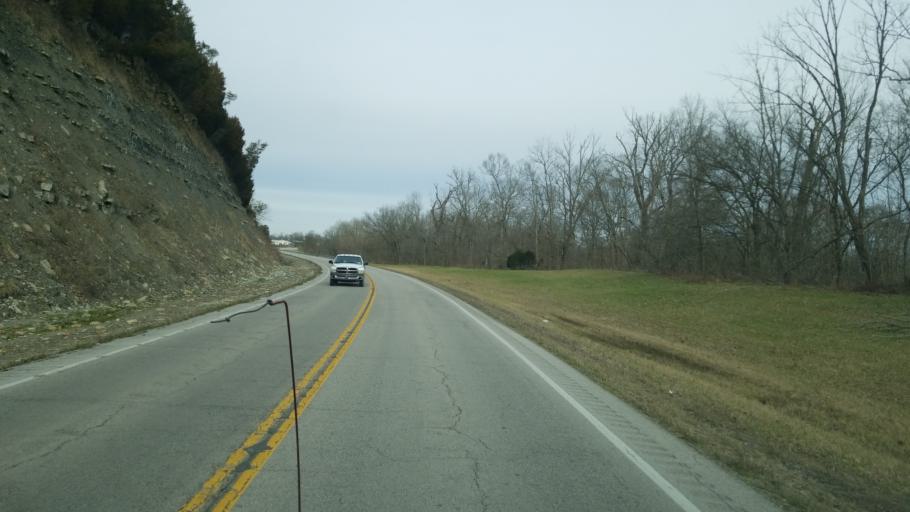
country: US
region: Kentucky
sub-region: Robertson County
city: Mount Olivet
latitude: 38.4312
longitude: -83.9913
